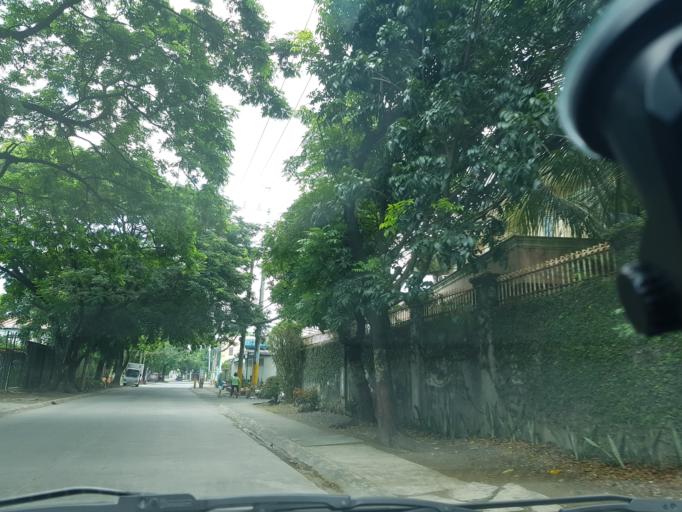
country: PH
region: Metro Manila
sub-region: Pasig
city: Pasig City
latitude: 14.5837
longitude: 121.0913
